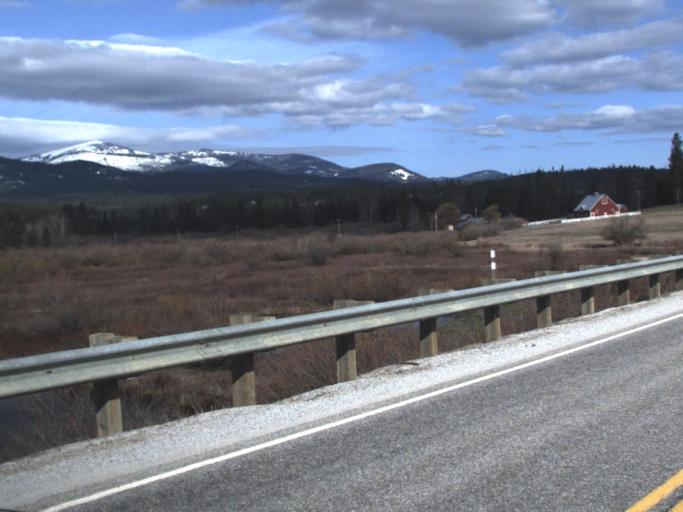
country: US
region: Washington
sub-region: Pend Oreille County
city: Newport
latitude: 48.3904
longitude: -117.3138
